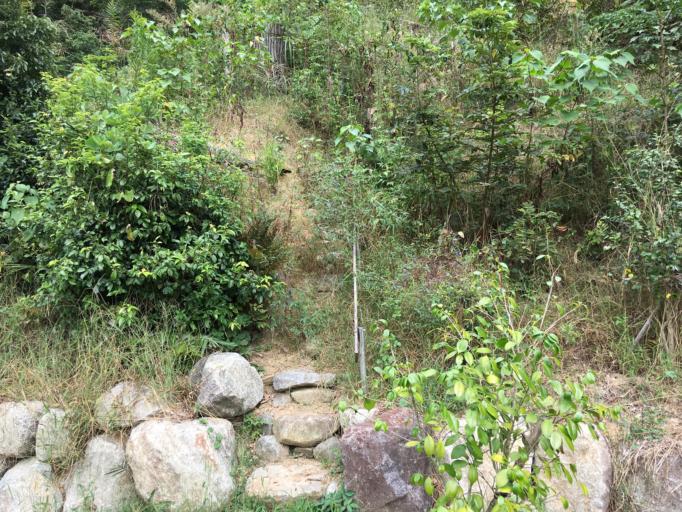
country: JP
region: Nara
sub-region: Ikoma-shi
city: Ikoma
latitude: 34.6724
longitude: 135.6974
